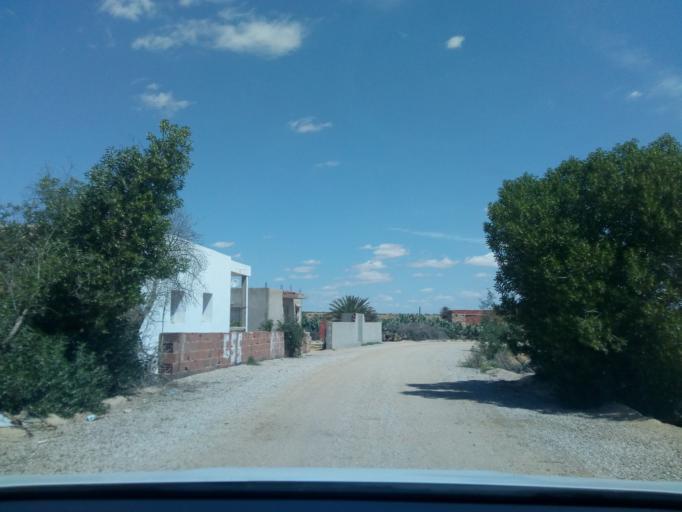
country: TN
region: Safaqis
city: Sfax
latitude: 34.7357
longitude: 10.4932
